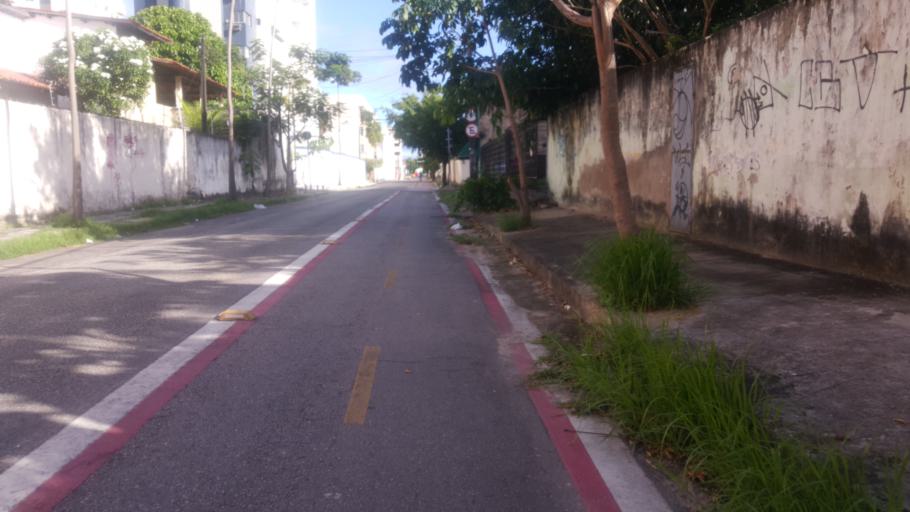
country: BR
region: Ceara
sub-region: Fortaleza
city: Fortaleza
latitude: -3.7467
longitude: -38.5397
